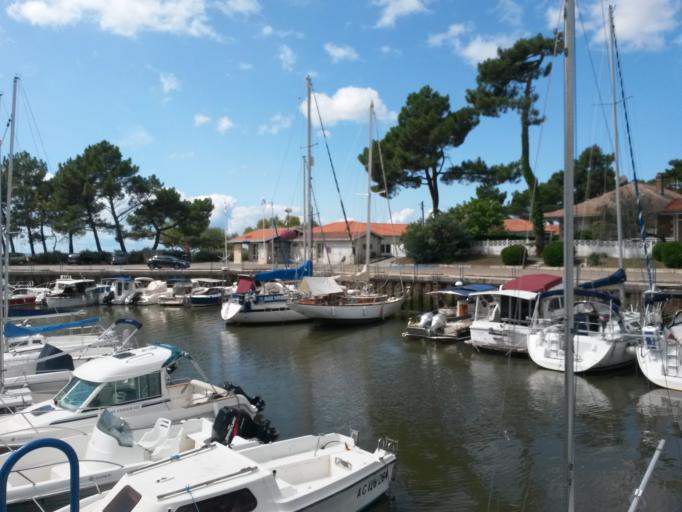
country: FR
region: Aquitaine
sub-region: Departement de la Gironde
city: Andernos-les-Bains
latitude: 44.7356
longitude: -1.0931
